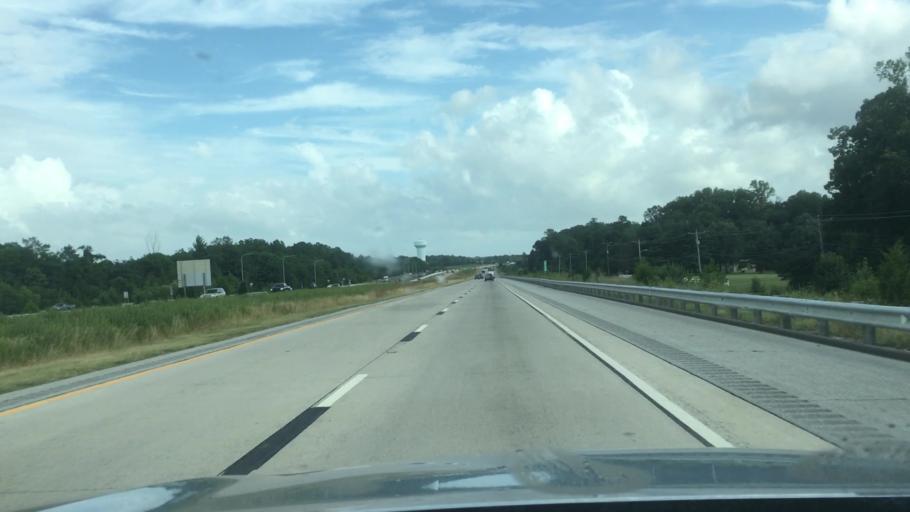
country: US
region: Delaware
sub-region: New Castle County
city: Townsend
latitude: 39.4369
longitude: -75.6614
